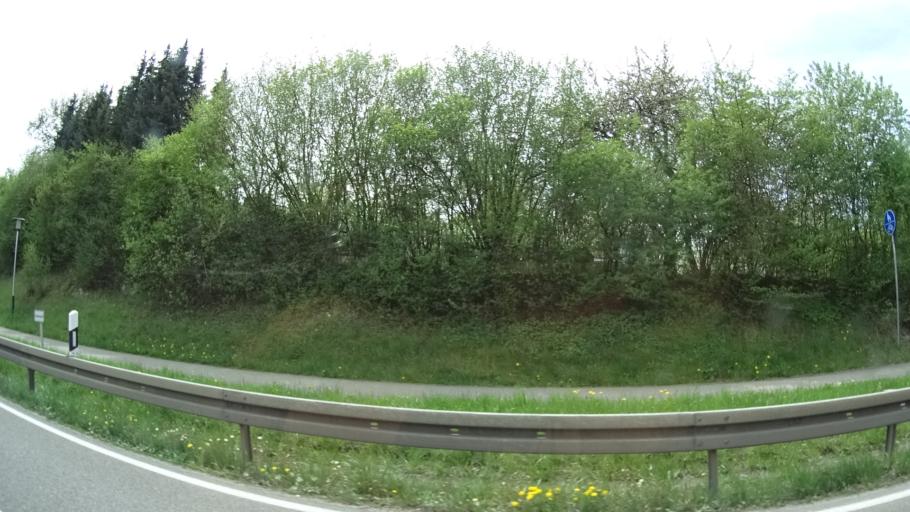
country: DE
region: Baden-Wuerttemberg
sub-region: Freiburg Region
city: Dauchingen
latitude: 48.0617
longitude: 8.5699
